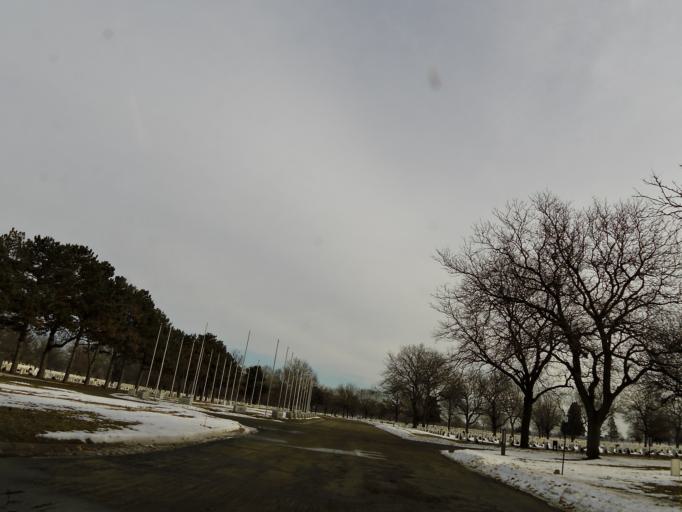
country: US
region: Minnesota
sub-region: Hennepin County
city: Richfield
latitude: 44.8720
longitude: -93.2201
